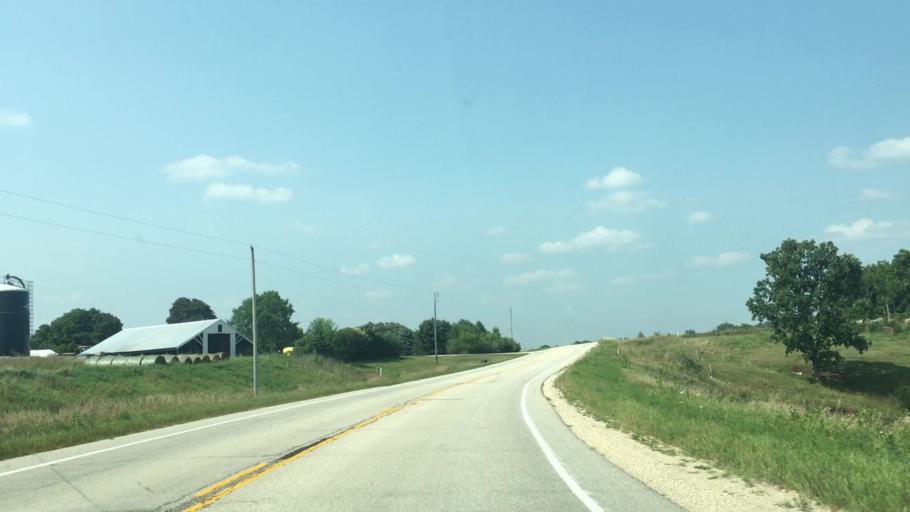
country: US
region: Minnesota
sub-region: Fillmore County
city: Preston
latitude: 43.6816
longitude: -91.9424
